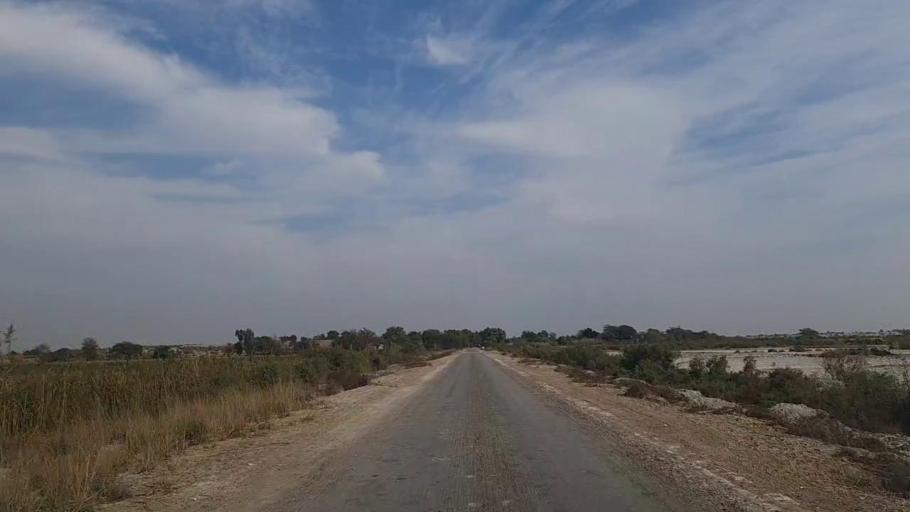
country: PK
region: Sindh
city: Daur
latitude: 26.4783
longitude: 68.4146
